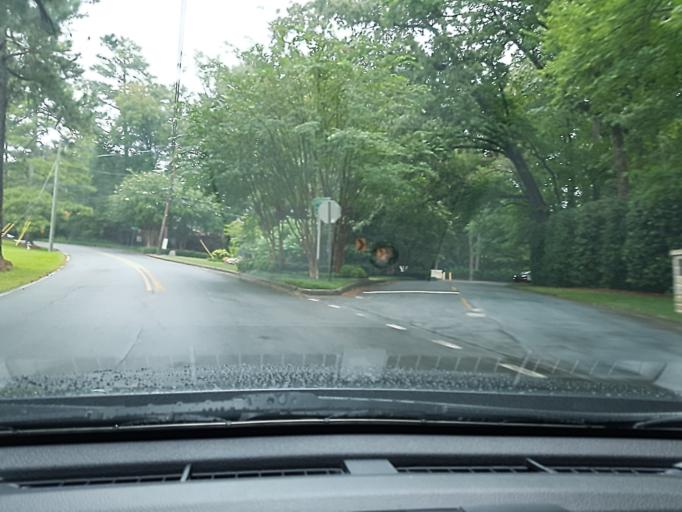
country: US
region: Georgia
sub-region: Cobb County
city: Vinings
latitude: 33.8651
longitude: -84.4128
